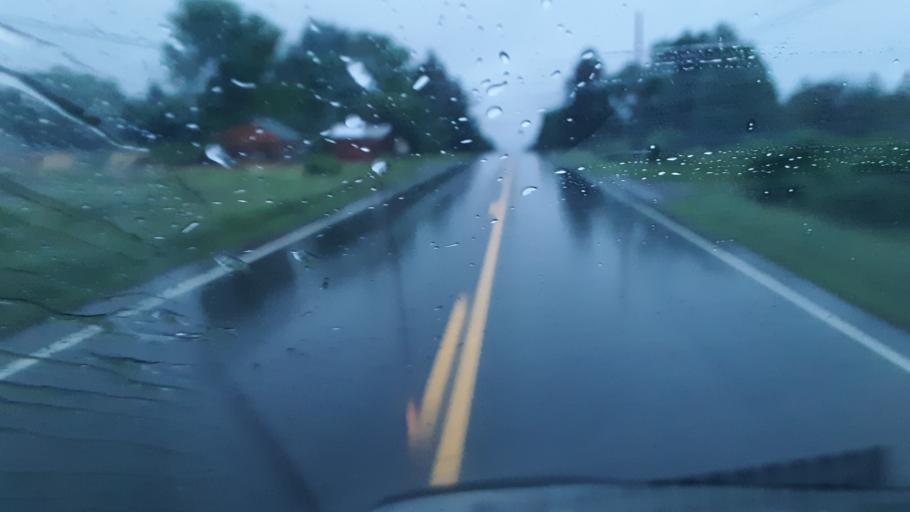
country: US
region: Maine
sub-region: Penobscot County
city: Patten
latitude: 45.9618
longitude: -68.4516
